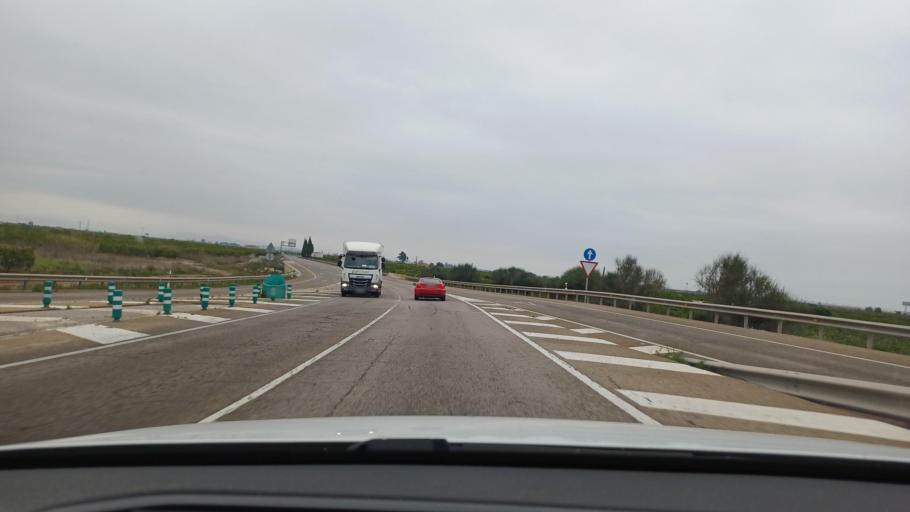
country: ES
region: Valencia
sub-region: Provincia de Castello
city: Nules
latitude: 39.8710
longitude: -0.1439
